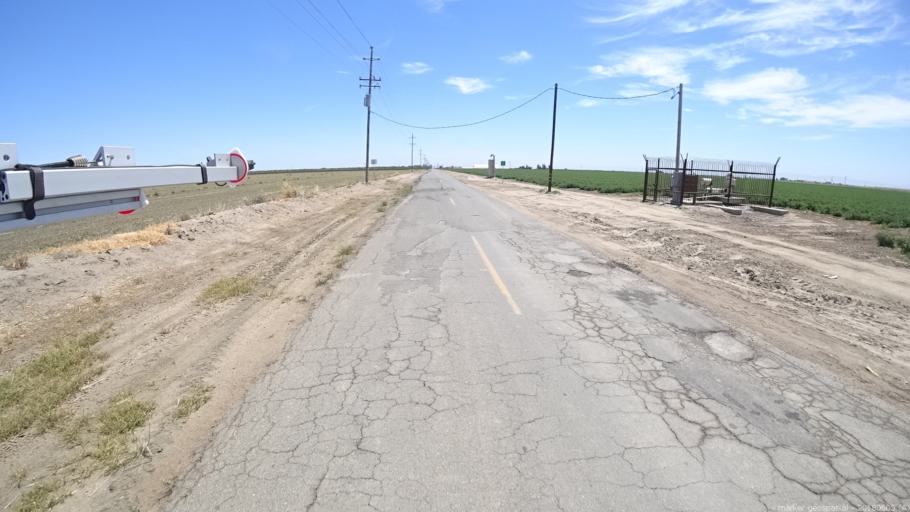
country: US
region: California
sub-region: Merced County
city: Dos Palos
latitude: 37.0953
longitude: -120.4734
